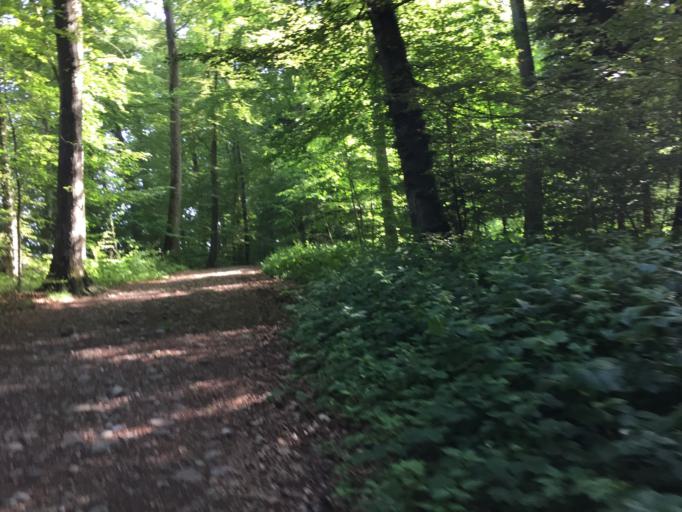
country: CH
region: Bern
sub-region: Bern-Mittelland District
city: Koniz
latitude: 46.9239
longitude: 7.3894
